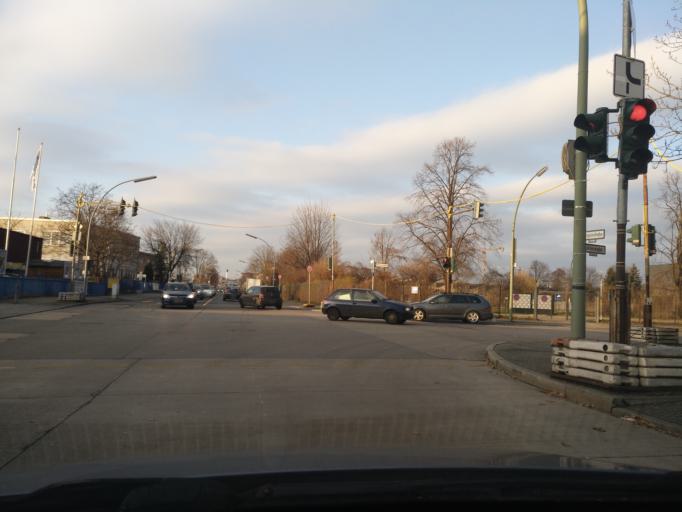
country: DE
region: Berlin
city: Plaenterwald
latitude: 52.4621
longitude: 13.4608
